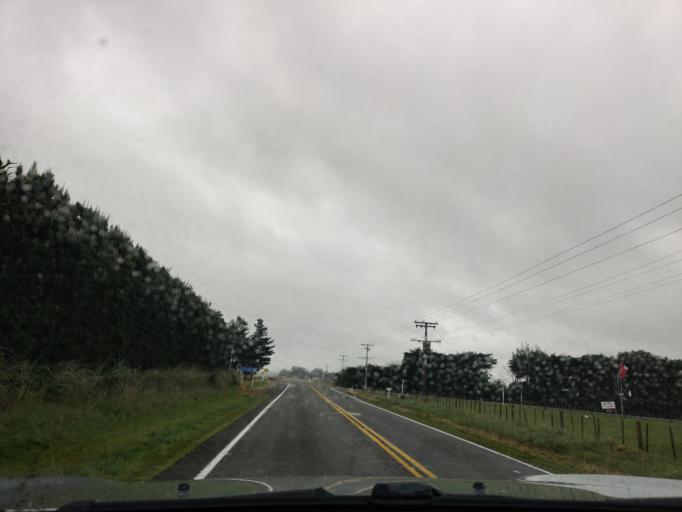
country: NZ
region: Hawke's Bay
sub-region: Hastings District
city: Hastings
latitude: -40.0166
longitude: 176.3547
